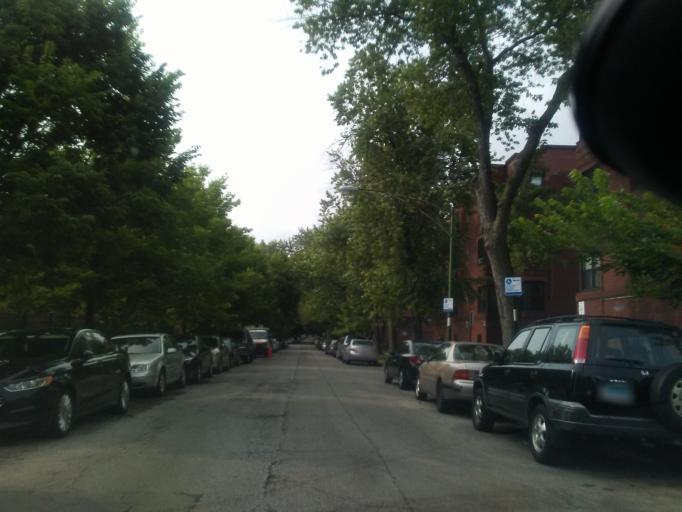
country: US
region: Illinois
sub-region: Cook County
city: Evanston
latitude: 41.9957
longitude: -87.6825
